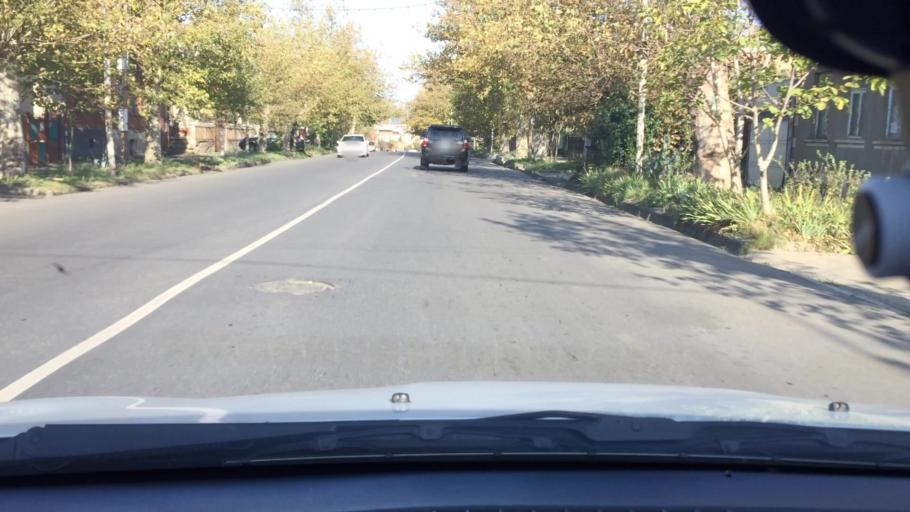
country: GE
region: Imereti
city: Kutaisi
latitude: 42.2683
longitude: 42.7162
